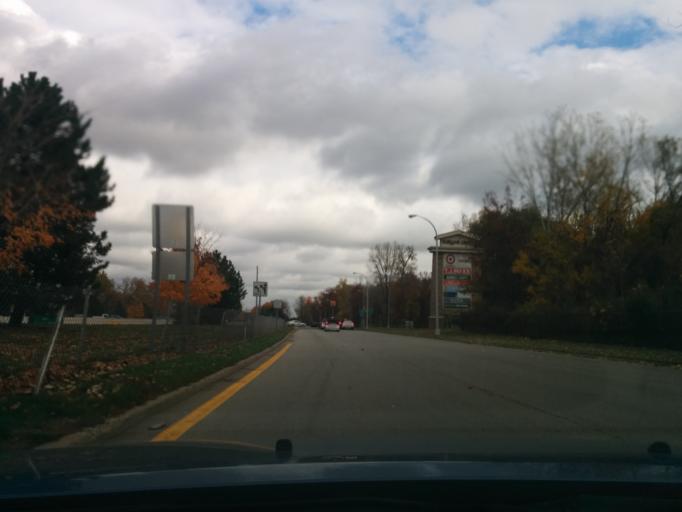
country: US
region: Michigan
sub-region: Wayne County
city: Allen Park
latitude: 42.2887
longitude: -83.2073
